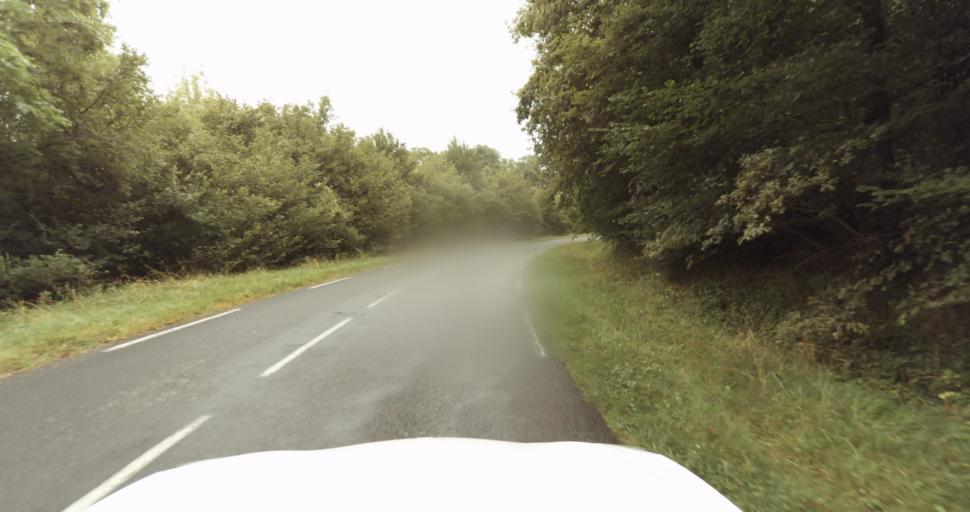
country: FR
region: Haute-Normandie
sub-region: Departement de l'Eure
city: Normanville
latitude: 49.0788
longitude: 1.1712
